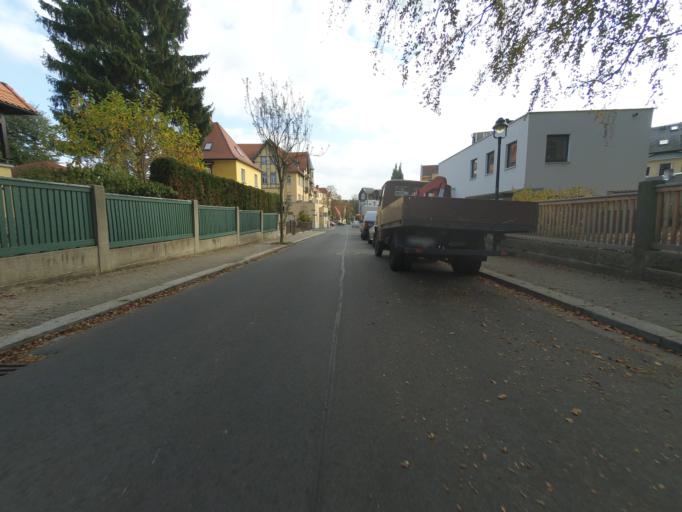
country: DE
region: Saxony
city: Radeberg
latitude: 51.0624
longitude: 13.8472
